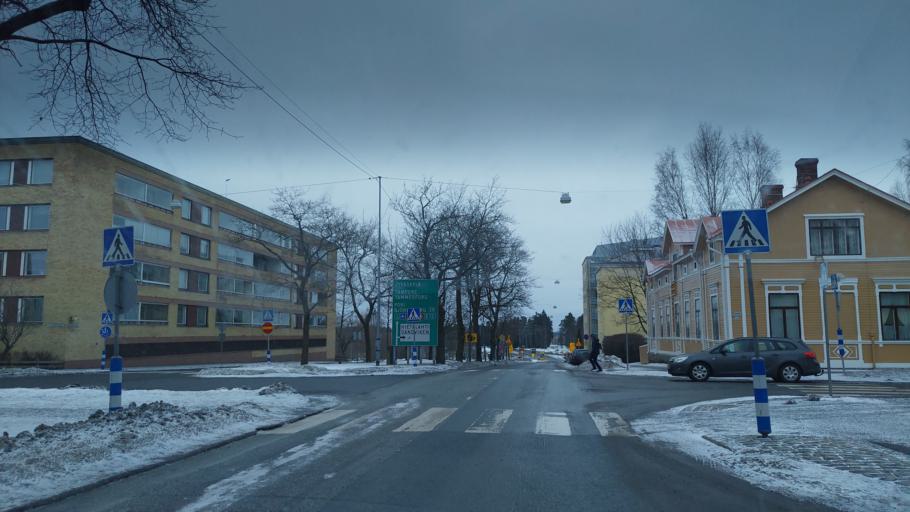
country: FI
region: Ostrobothnia
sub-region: Vaasa
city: Vaasa
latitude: 63.0892
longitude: 21.6215
